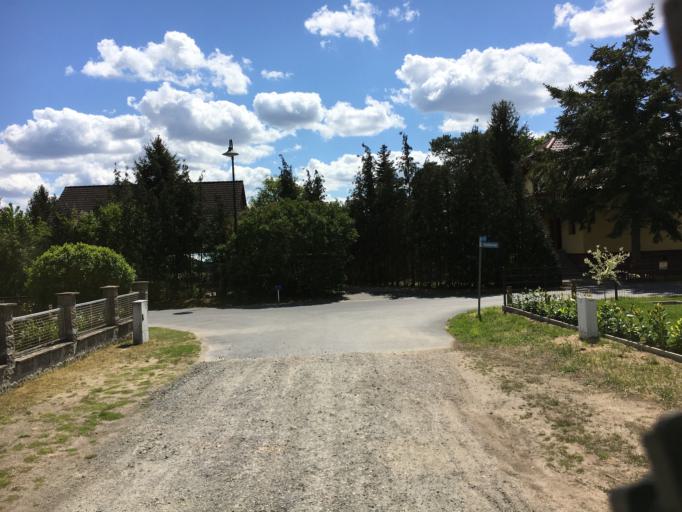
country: DE
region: Brandenburg
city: Luckenwalde
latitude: 52.1298
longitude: 13.1714
